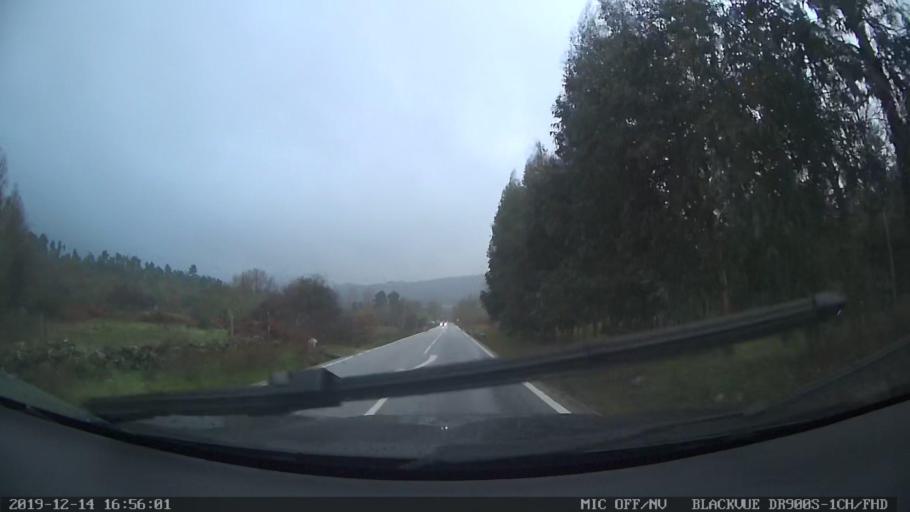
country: PT
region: Vila Real
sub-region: Murca
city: Murca
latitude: 41.4368
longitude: -7.5358
